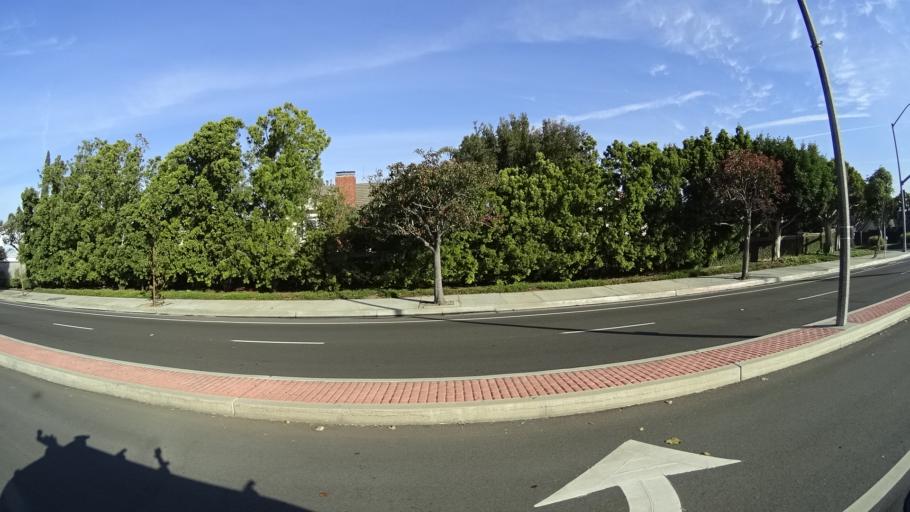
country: US
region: California
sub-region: Los Angeles County
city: Manhattan Beach
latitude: 33.8946
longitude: -118.3923
